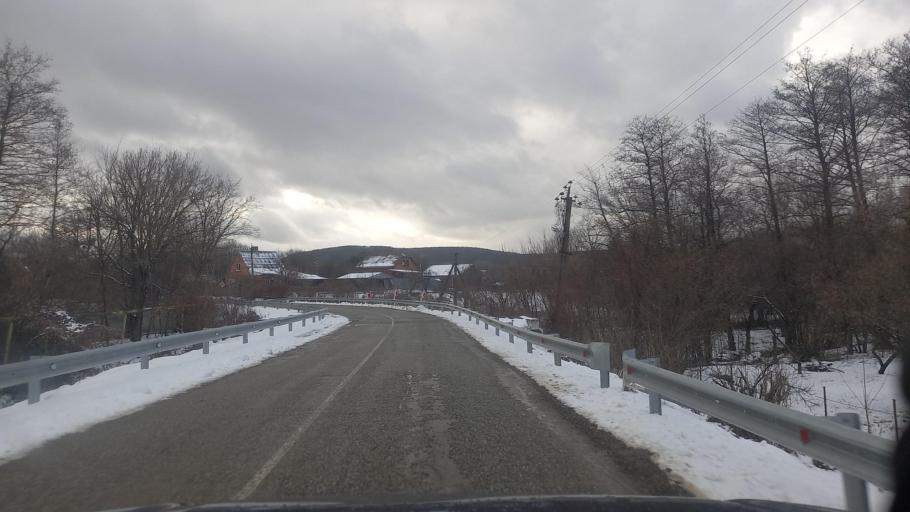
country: RU
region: Krasnodarskiy
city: Smolenskaya
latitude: 44.7224
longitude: 38.8275
